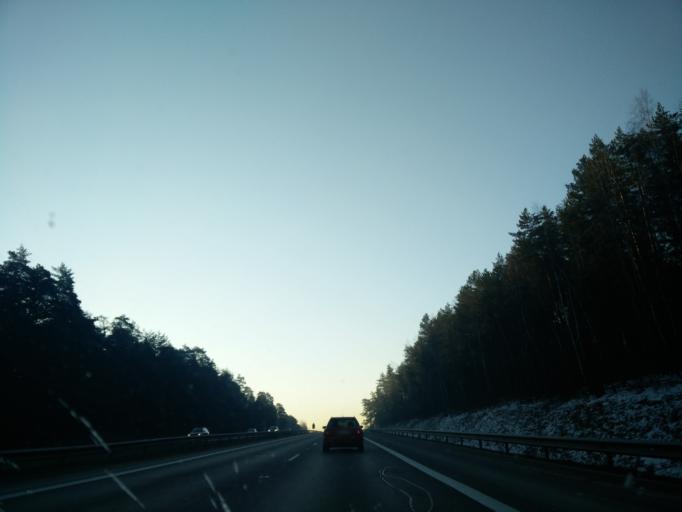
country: LT
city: Grigiskes
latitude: 54.6659
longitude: 25.1188
